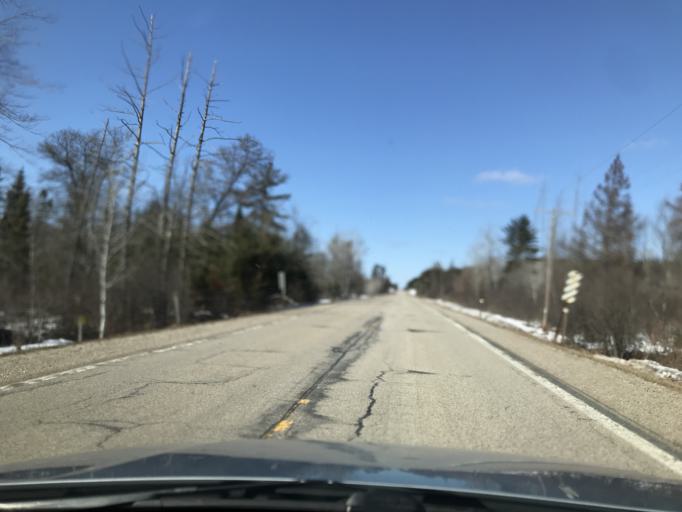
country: US
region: Wisconsin
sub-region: Marinette County
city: Niagara
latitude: 45.3708
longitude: -88.1001
